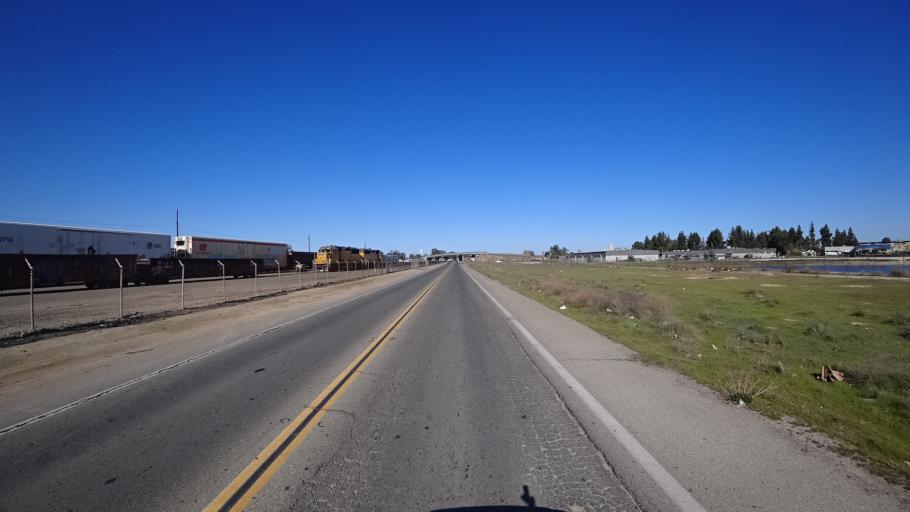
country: US
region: California
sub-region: Fresno County
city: West Park
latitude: 36.7907
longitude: -119.8556
